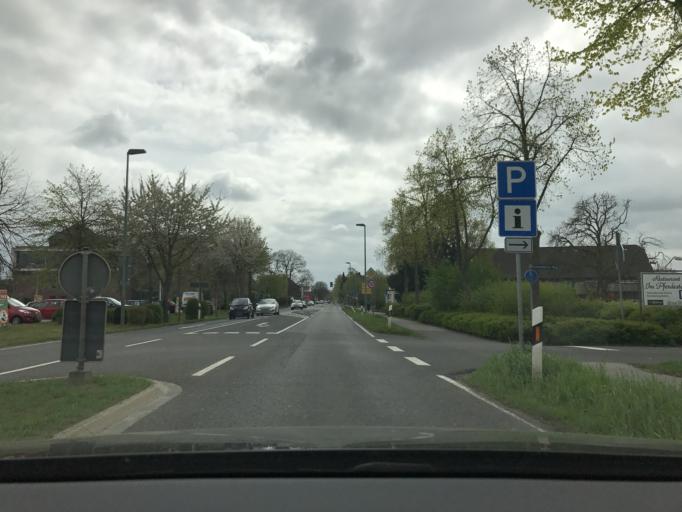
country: DE
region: North Rhine-Westphalia
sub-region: Regierungsbezirk Dusseldorf
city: Kaarst
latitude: 51.2791
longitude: 6.6146
